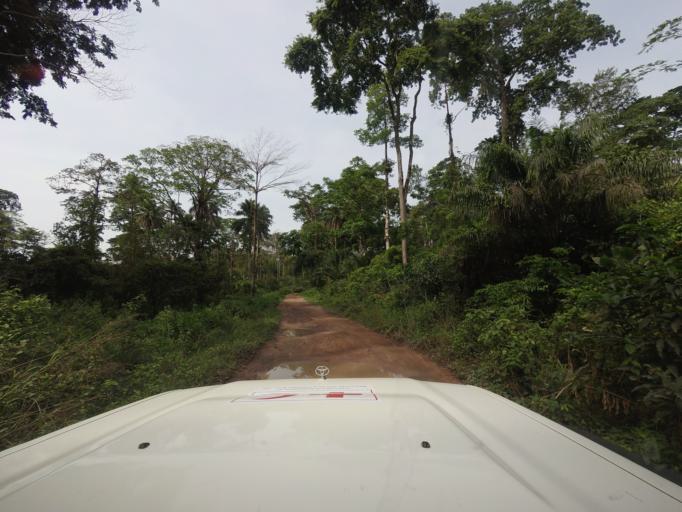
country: GN
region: Nzerekore
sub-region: Macenta
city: Macenta
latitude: 8.4855
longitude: -9.5420
